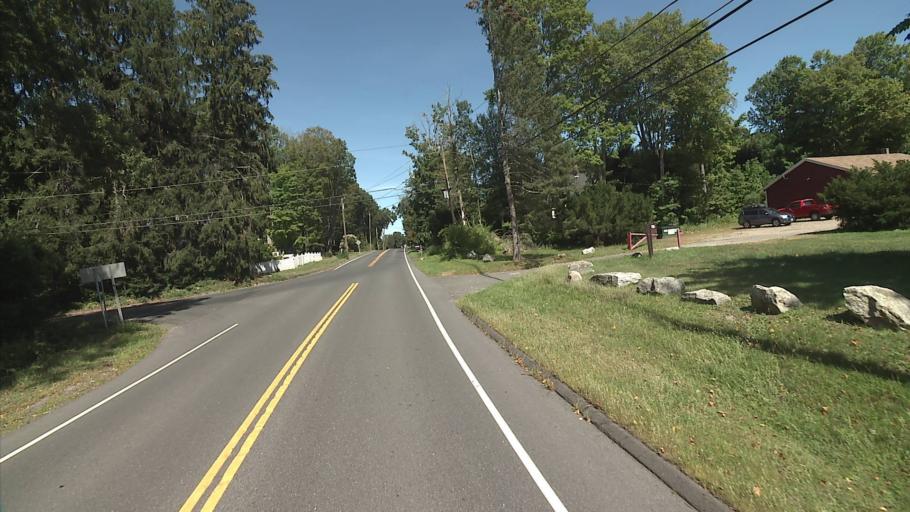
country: US
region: Connecticut
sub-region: New Haven County
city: Southbury
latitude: 41.4596
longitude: -73.1646
